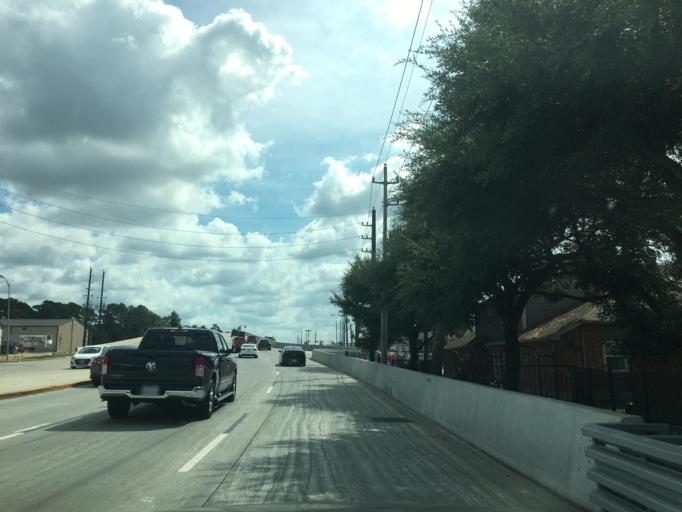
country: US
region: Texas
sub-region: Montgomery County
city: Oak Ridge North
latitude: 30.1273
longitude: -95.4320
